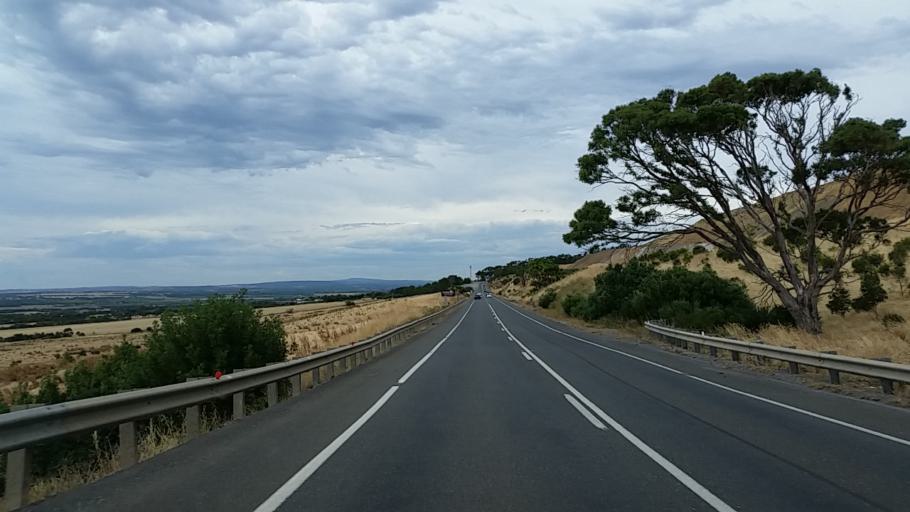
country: AU
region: South Australia
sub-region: Onkaparinga
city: Aldinga
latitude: -35.3446
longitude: 138.4580
